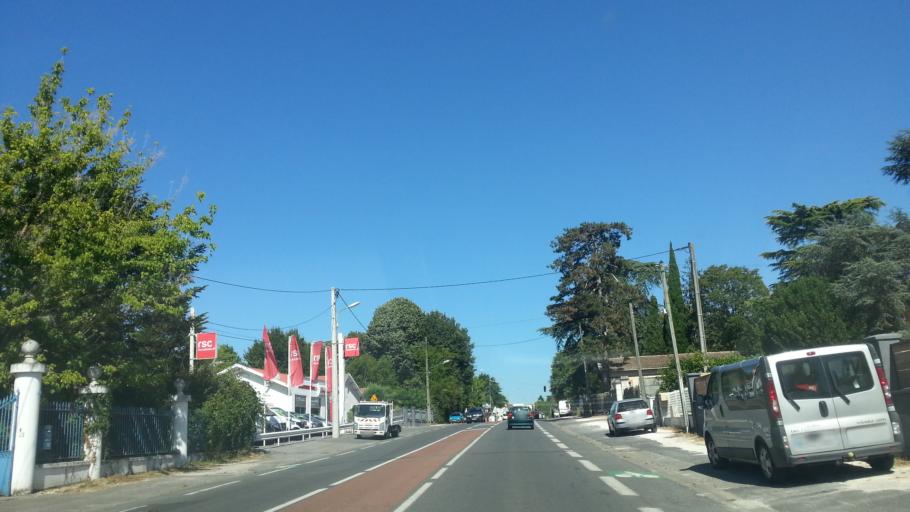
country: FR
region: Aquitaine
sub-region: Departement de la Gironde
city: Villenave-d'Ornon
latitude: 44.7609
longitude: -0.5573
